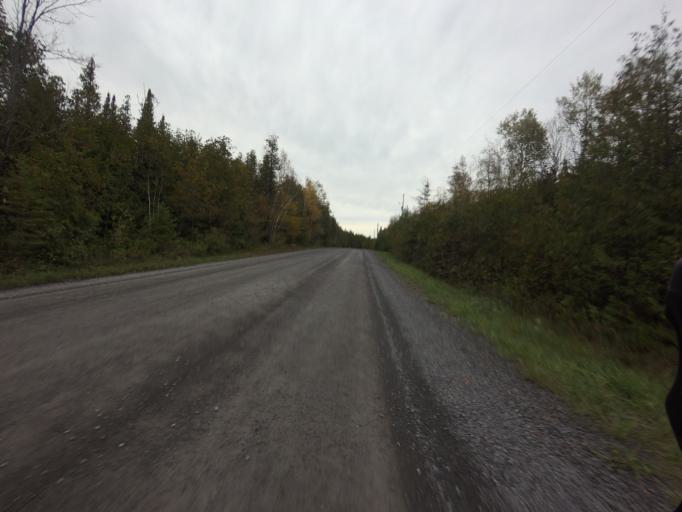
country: CA
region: Ontario
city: Bells Corners
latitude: 45.0663
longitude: -75.7616
